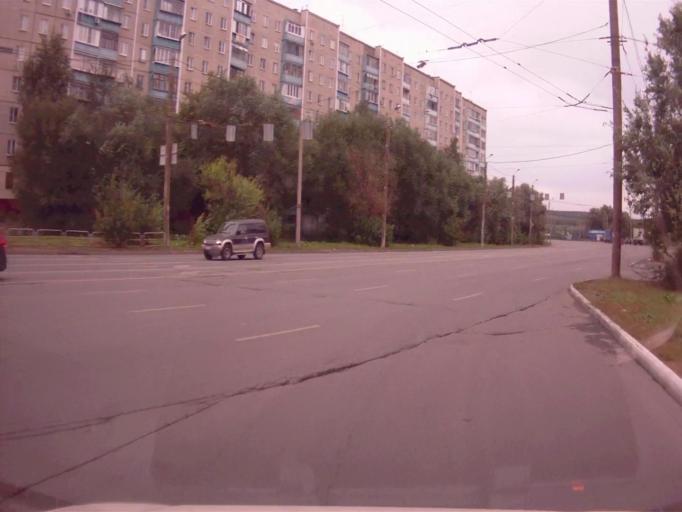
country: RU
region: Chelyabinsk
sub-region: Gorod Chelyabinsk
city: Chelyabinsk
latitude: 55.1753
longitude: 61.3344
